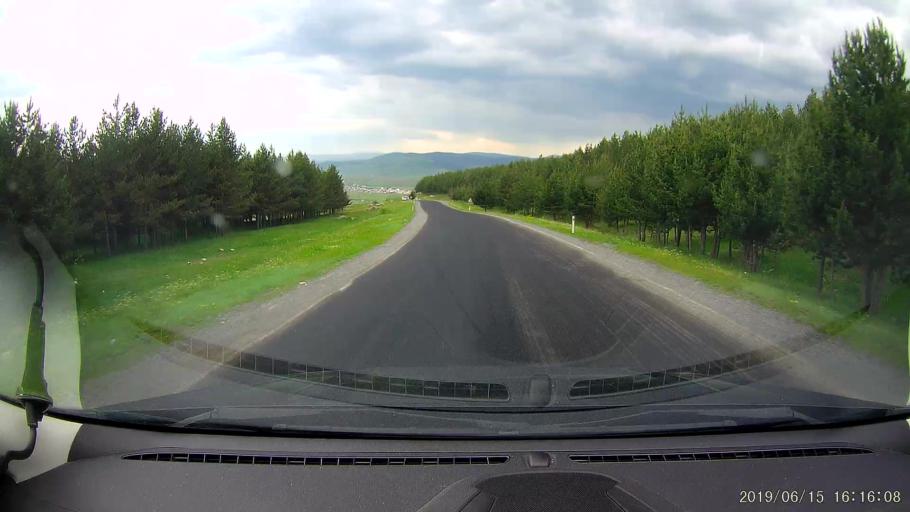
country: TR
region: Ardahan
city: Hanak
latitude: 41.2618
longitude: 42.8529
